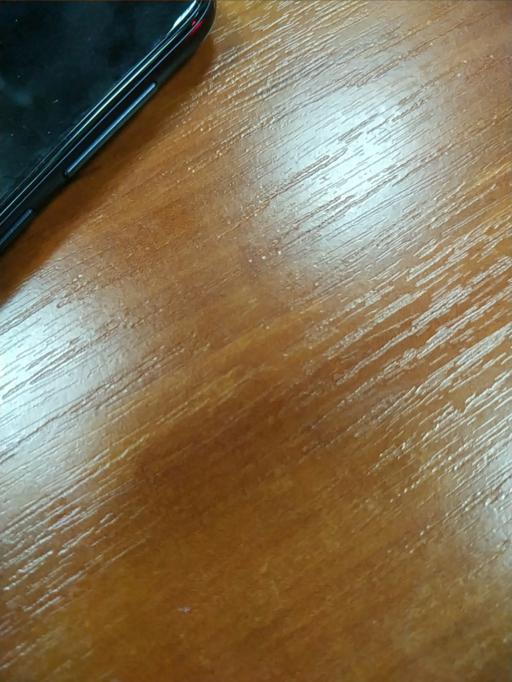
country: RU
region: Moskovskaya
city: Dolgoprudnyy
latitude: 55.9525
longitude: 37.5038
